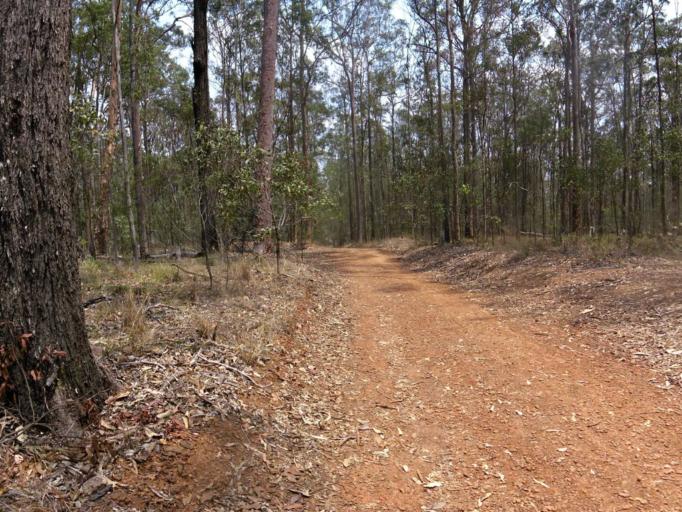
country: AU
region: Queensland
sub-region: Logan
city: Springwood
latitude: -27.6103
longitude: 153.1570
